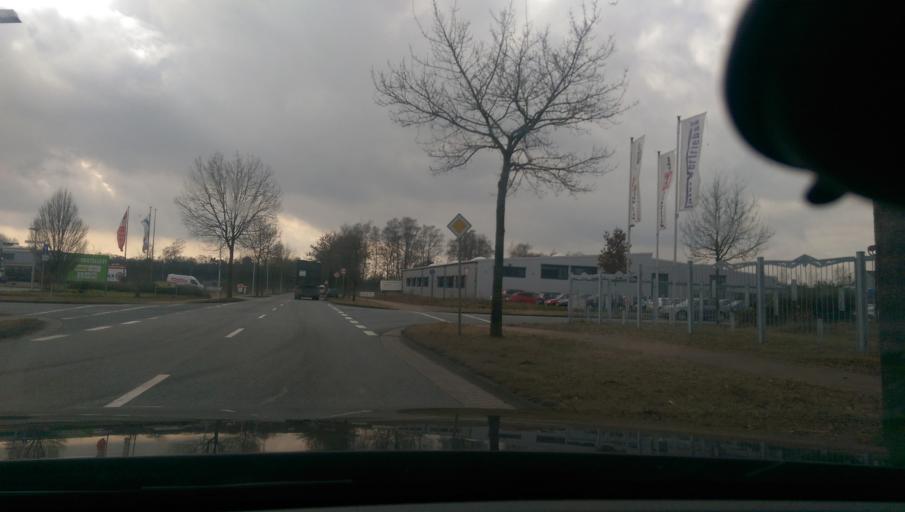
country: DE
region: Lower Saxony
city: Kirchlinteln
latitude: 52.9221
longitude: 9.2866
